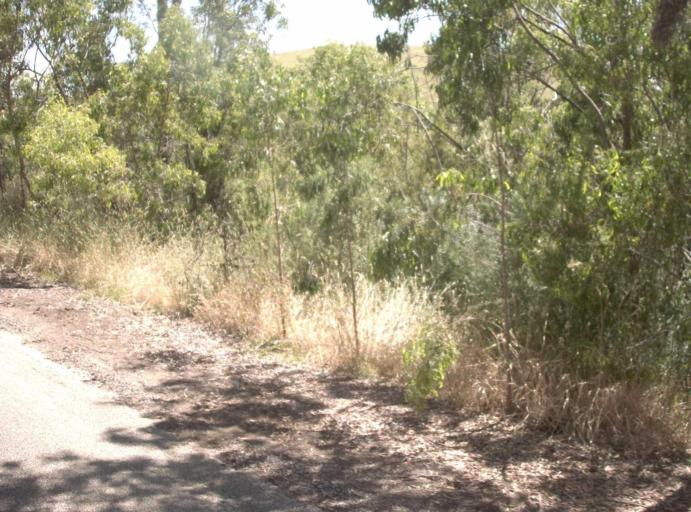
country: AU
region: Victoria
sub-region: East Gippsland
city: Lakes Entrance
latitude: -37.4494
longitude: 148.1921
